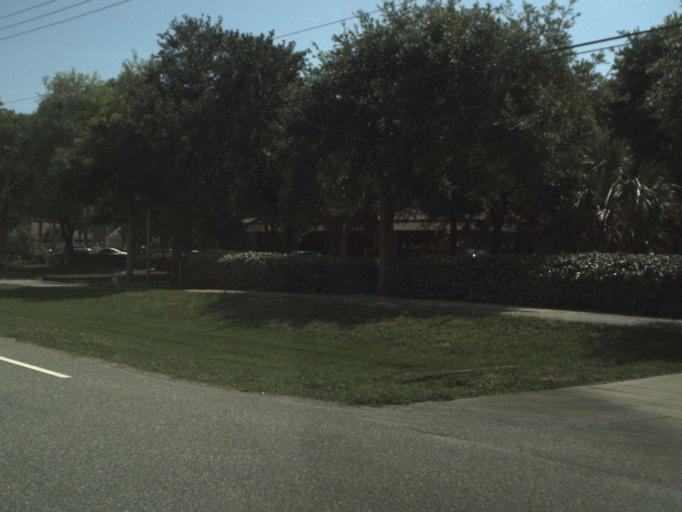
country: US
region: Florida
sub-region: Volusia County
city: Port Orange
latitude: 29.1305
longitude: -81.0021
